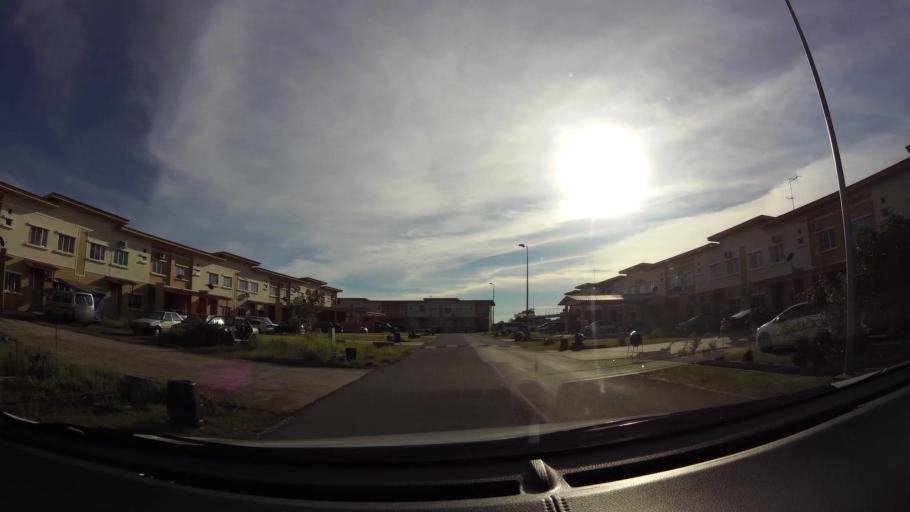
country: BN
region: Belait
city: Kuala Belait
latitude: 4.5796
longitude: 114.2215
